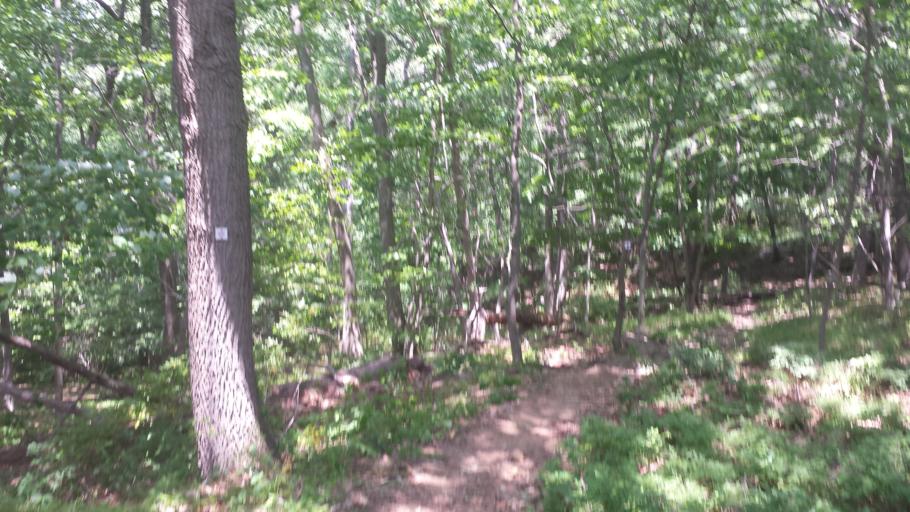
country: US
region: New York
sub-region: Westchester County
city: Valhalla
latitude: 41.0743
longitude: -73.7537
